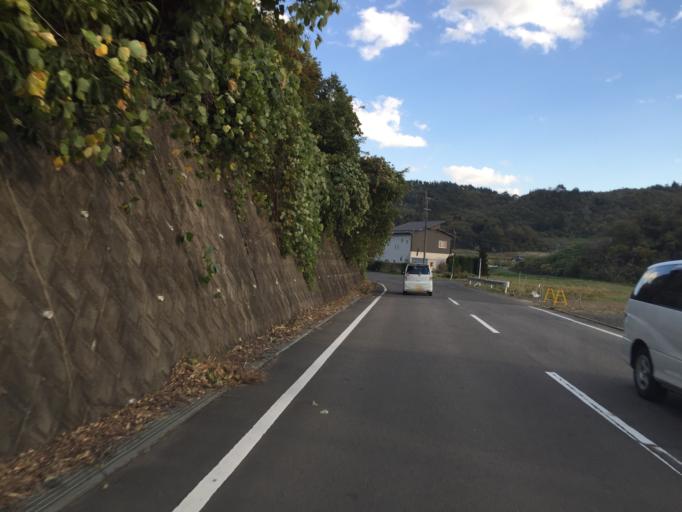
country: JP
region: Fukushima
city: Fukushima-shi
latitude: 37.7023
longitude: 140.4214
